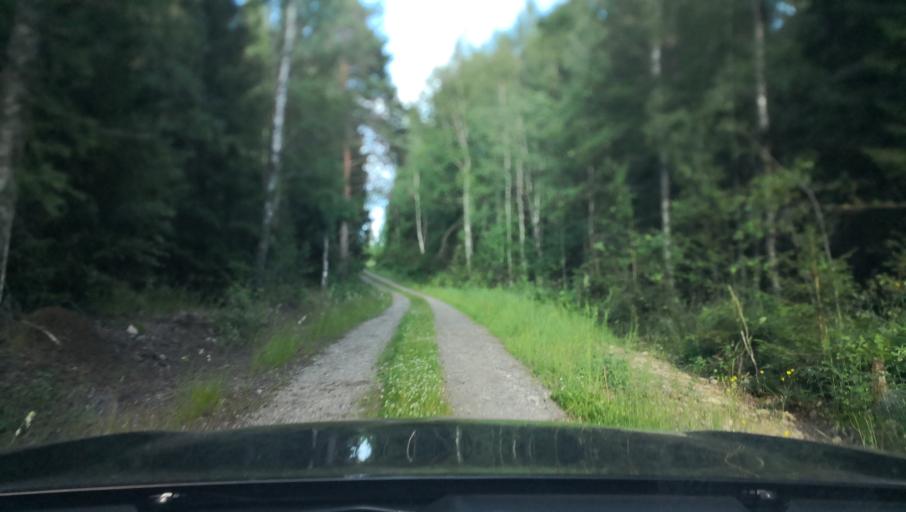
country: SE
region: Dalarna
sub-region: Ludvika Kommun
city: Ludvika
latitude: 60.0747
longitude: 15.2704
